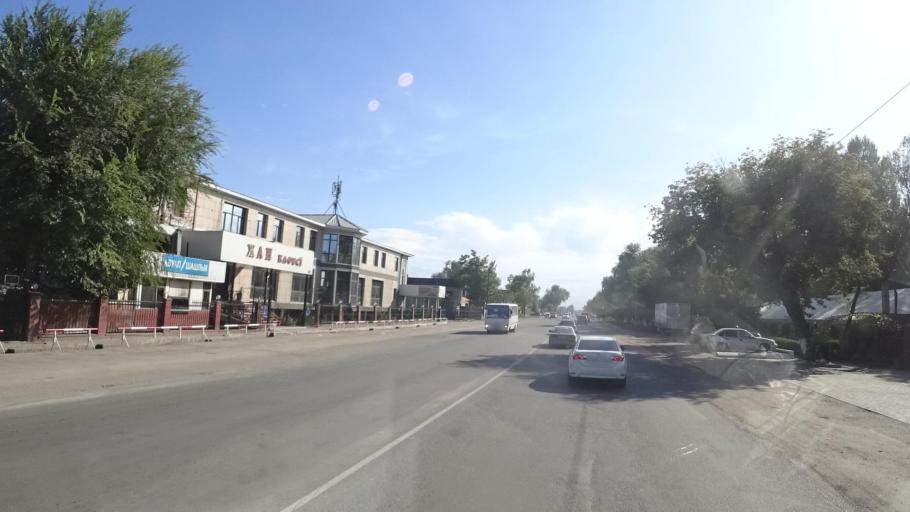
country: KZ
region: Almaty Oblysy
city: Energeticheskiy
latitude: 43.4253
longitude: 77.0245
